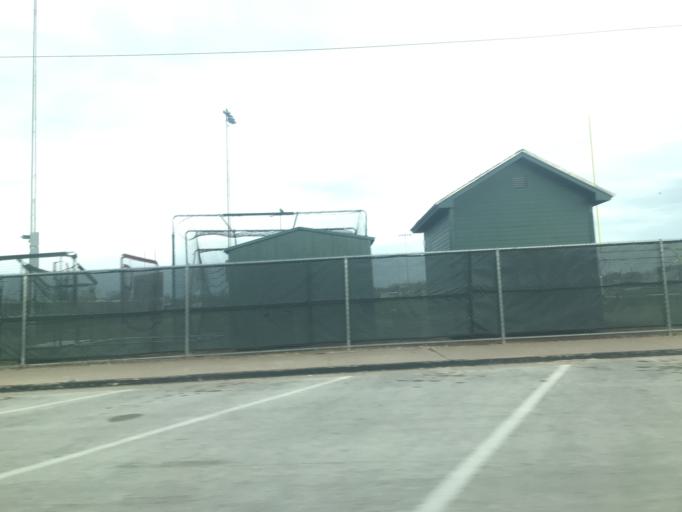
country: US
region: Texas
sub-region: Taylor County
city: Abilene
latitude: 32.4581
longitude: -99.7576
